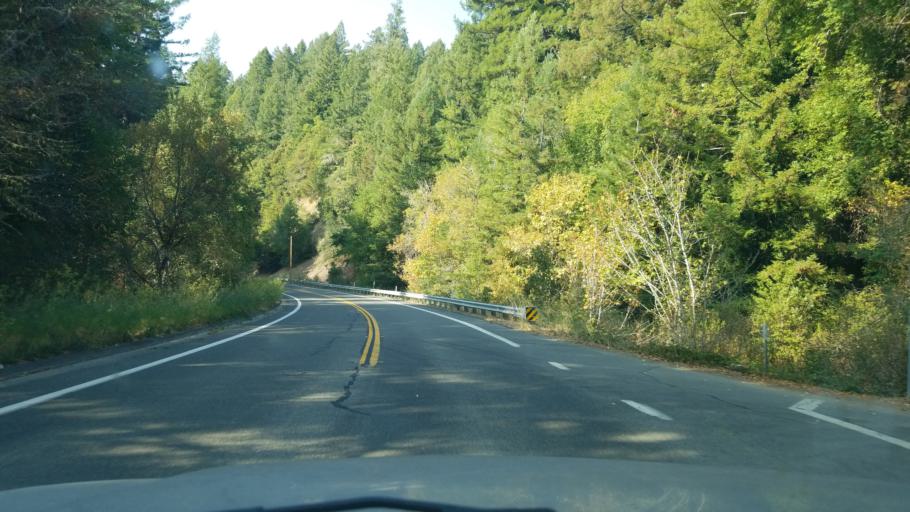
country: US
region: California
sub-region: Humboldt County
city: Redway
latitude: 40.2193
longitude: -123.7860
